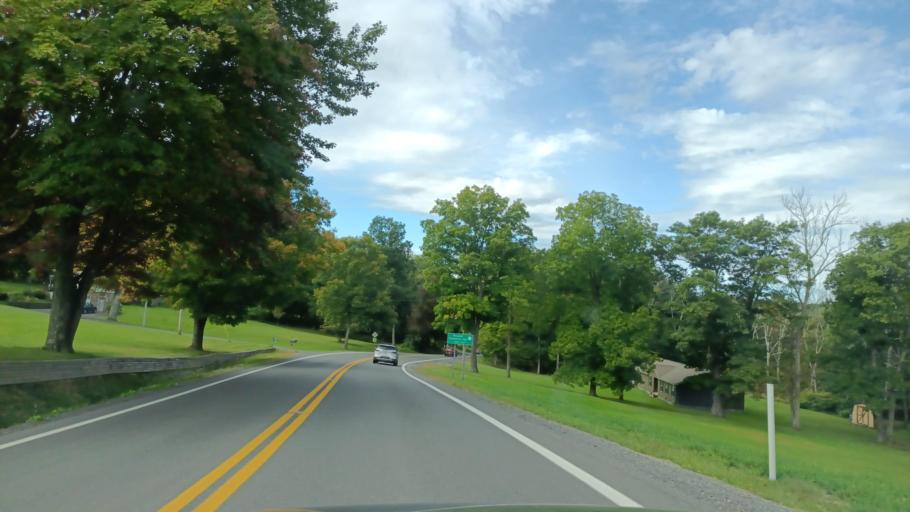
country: US
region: Maryland
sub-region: Garrett County
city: Mountain Lake Park
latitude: 39.2874
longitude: -79.3223
